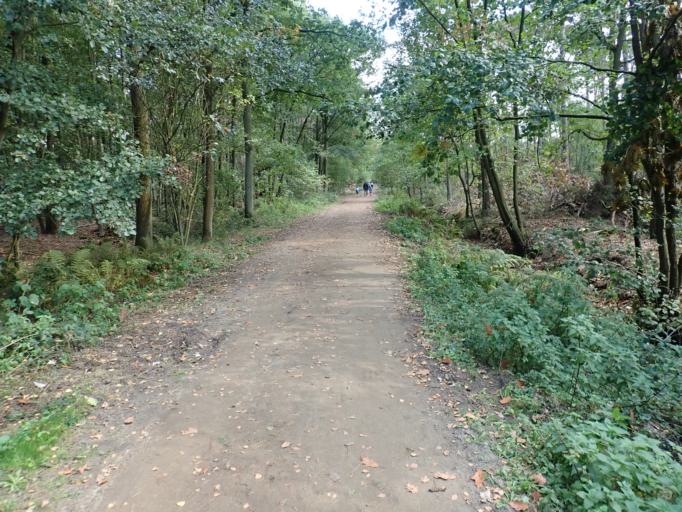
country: BE
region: Flanders
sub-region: Provincie Oost-Vlaanderen
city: Sint-Gillis-Waas
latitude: 51.2422
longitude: 4.0845
